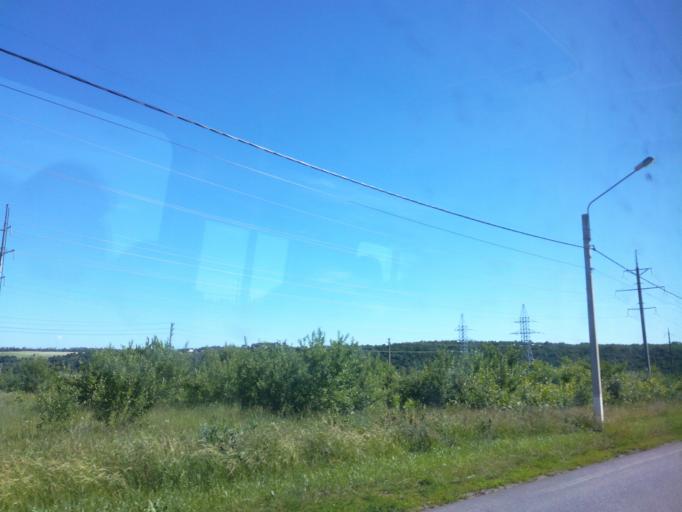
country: RU
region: Kursk
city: Kursk
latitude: 51.7932
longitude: 36.1863
